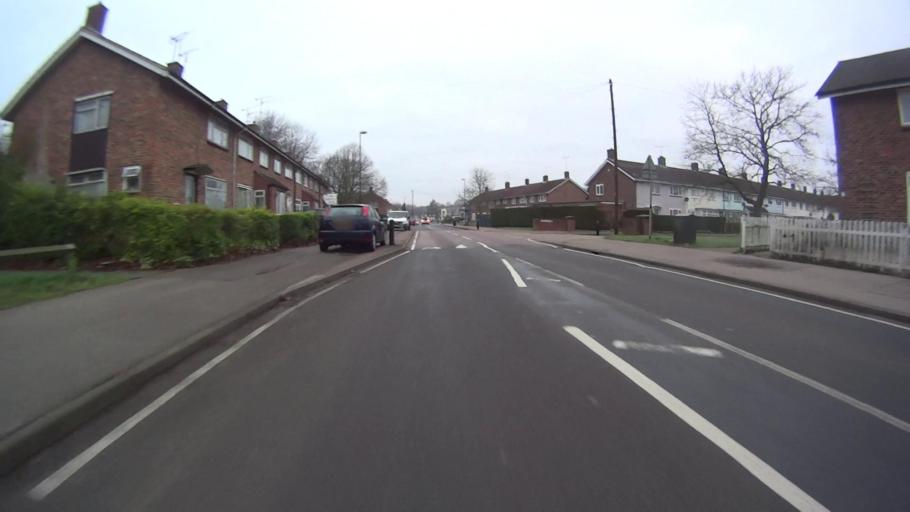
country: GB
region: England
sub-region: West Sussex
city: Furnace Green
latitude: 51.1022
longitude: -0.1770
